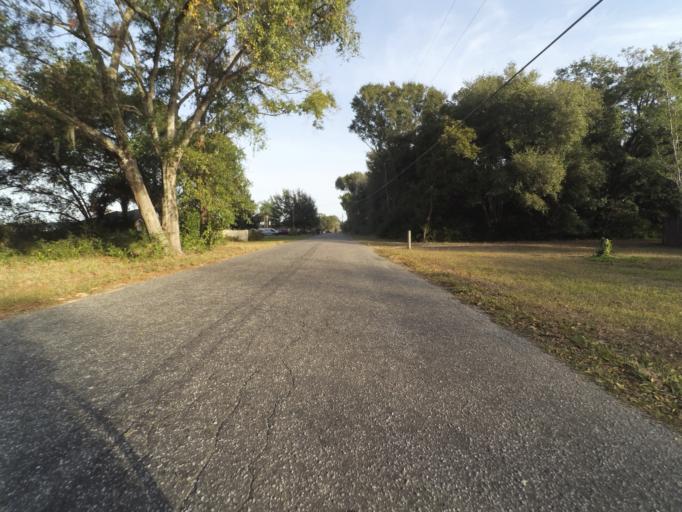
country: US
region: Florida
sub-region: Lake County
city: Umatilla
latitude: 28.9369
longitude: -81.6569
